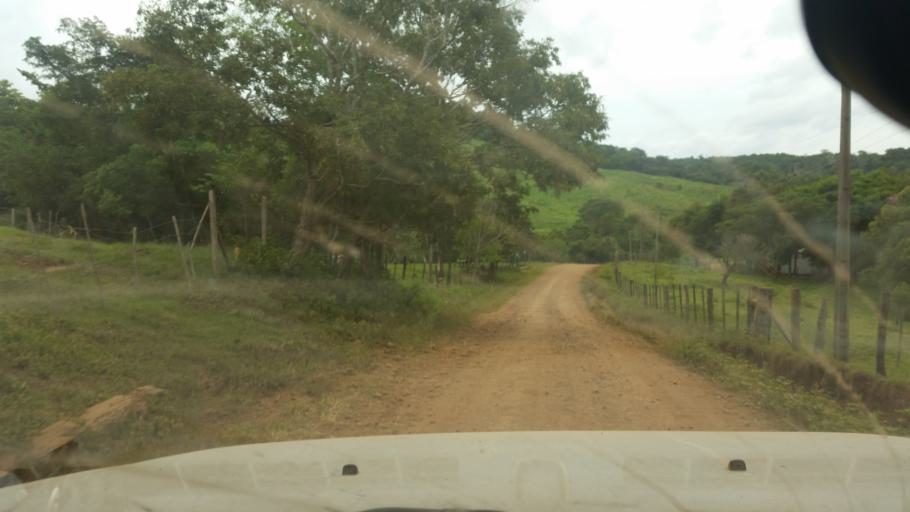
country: PY
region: Guaira
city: Independencia
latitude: -25.7809
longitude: -56.2557
